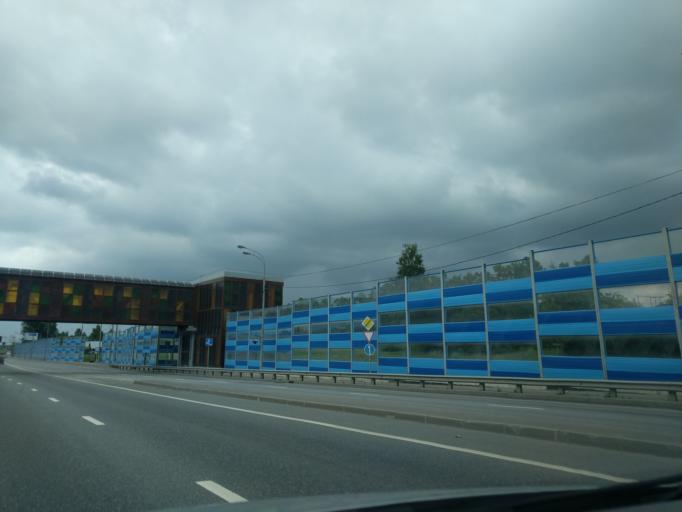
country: RU
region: Moscow
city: Severnyy
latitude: 55.9359
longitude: 37.5463
